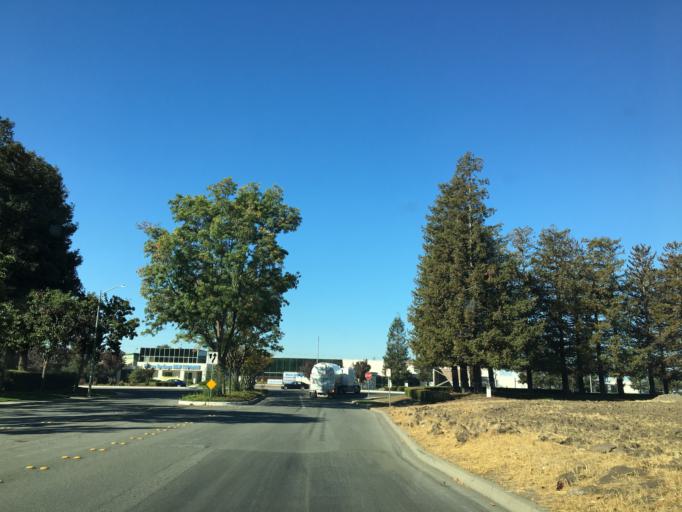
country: US
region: California
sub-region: Santa Clara County
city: Milpitas
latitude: 37.4976
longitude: -121.9333
